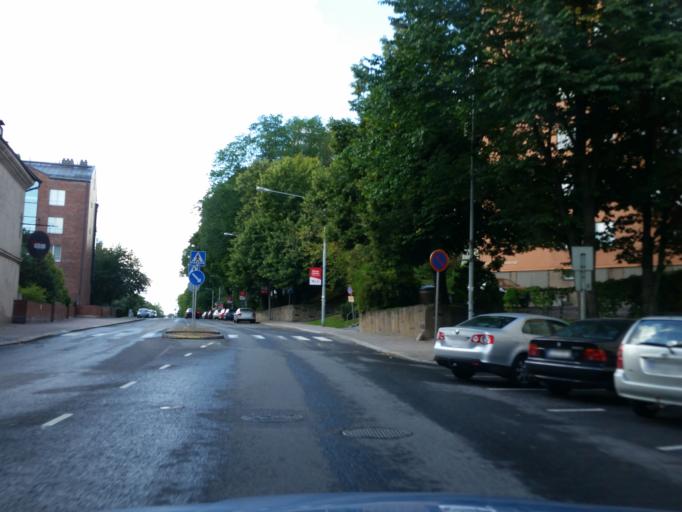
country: FI
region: Varsinais-Suomi
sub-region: Turku
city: Turku
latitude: 60.4437
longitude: 22.2511
